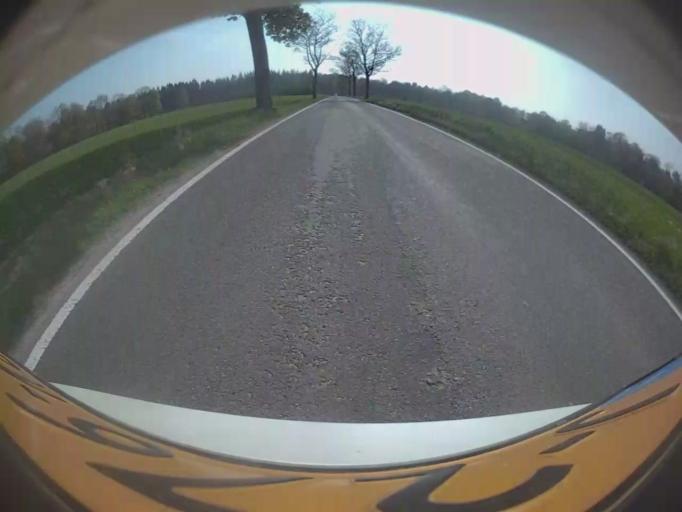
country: BE
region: Wallonia
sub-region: Province de Namur
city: Hamois
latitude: 50.3012
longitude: 5.2151
